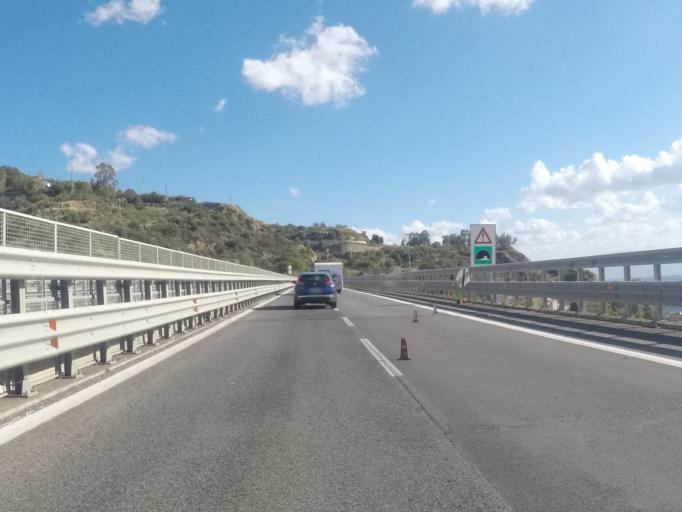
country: IT
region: Sicily
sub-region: Messina
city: Ali Terme
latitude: 38.0079
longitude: 15.4236
